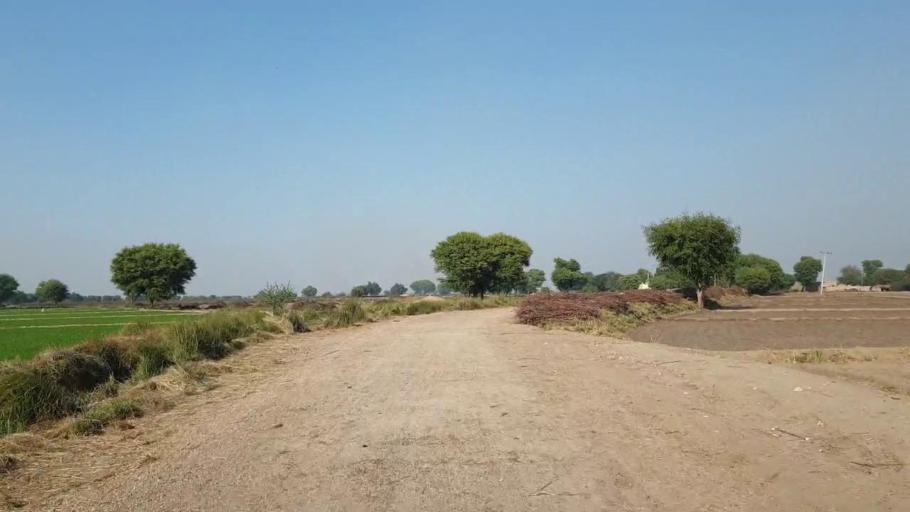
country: PK
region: Sindh
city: Sehwan
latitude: 26.4594
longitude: 67.8152
